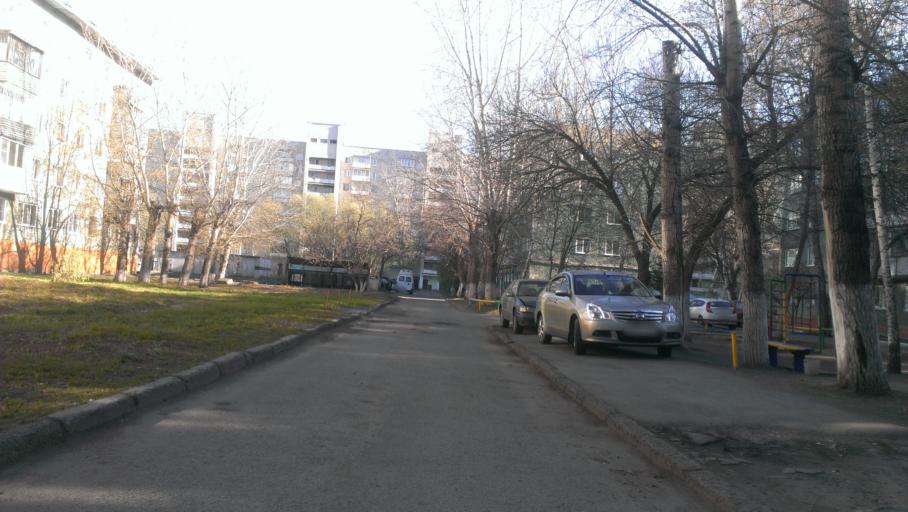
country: RU
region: Altai Krai
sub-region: Gorod Barnaulskiy
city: Barnaul
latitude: 53.3442
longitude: 83.6922
